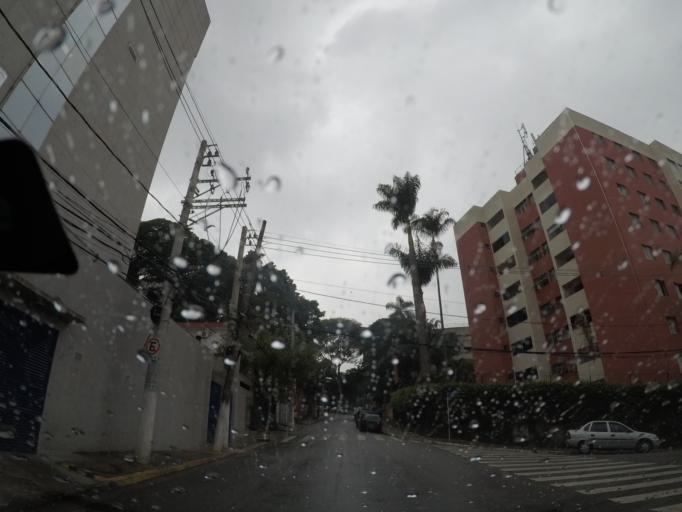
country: BR
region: Sao Paulo
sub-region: Diadema
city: Diadema
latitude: -23.6441
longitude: -46.6435
